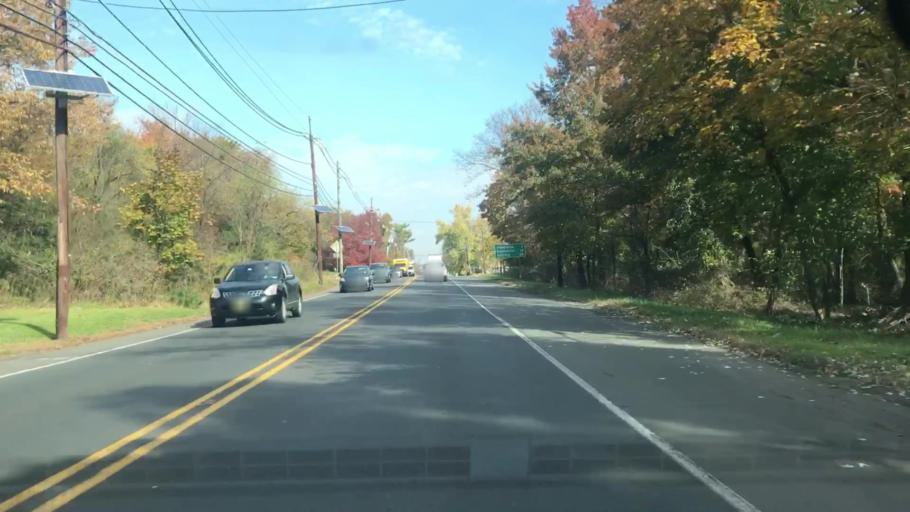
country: US
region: New Jersey
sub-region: Somerset County
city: Weston
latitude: 40.5313
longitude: -74.6233
